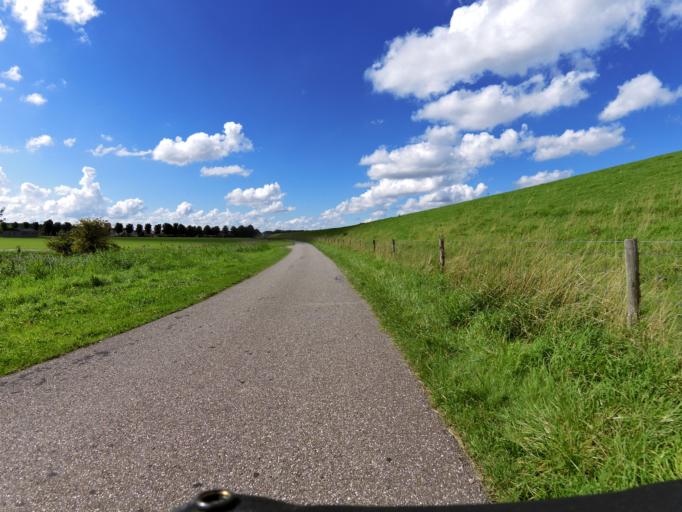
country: NL
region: North Brabant
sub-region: Gemeente Steenbergen
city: Dinteloord
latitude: 51.7171
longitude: 4.2954
